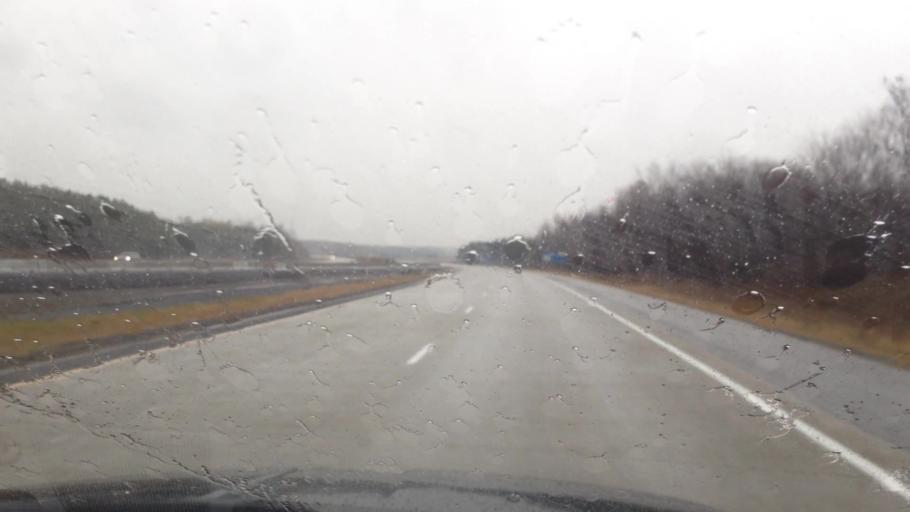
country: CA
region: Ontario
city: Hawkesbury
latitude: 45.4494
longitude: -74.7066
